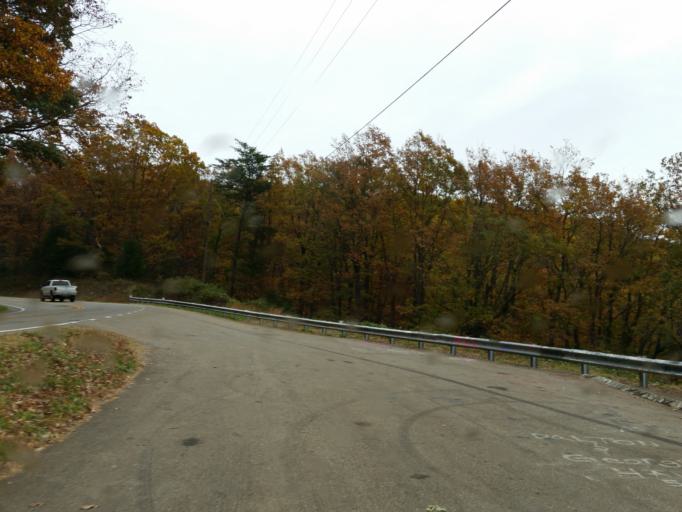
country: US
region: Georgia
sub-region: Pickens County
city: Jasper
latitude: 34.5337
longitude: -84.3776
